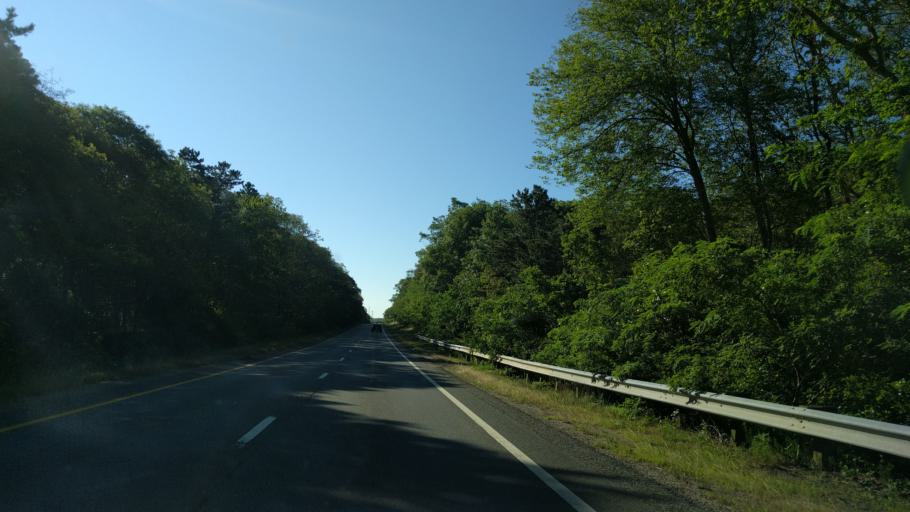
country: US
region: Massachusetts
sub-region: Barnstable County
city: West Barnstable
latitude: 41.6996
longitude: -70.3914
